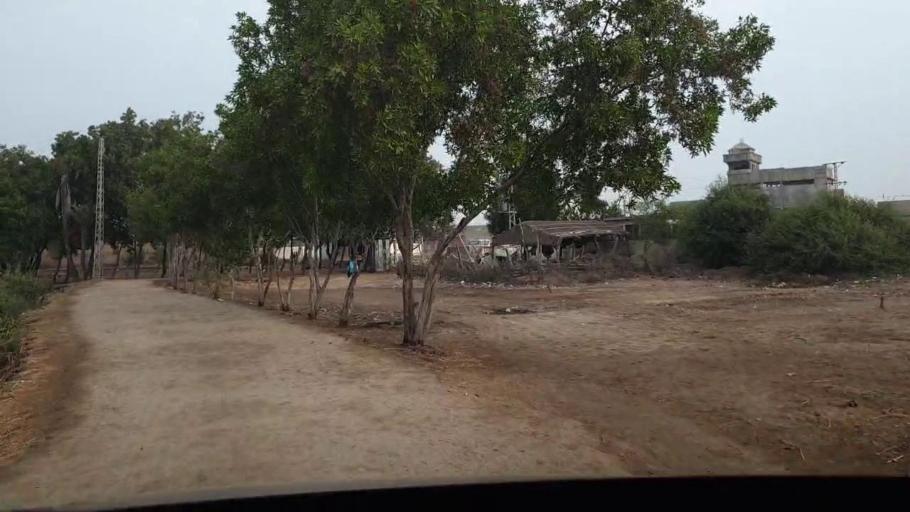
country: PK
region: Sindh
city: Thatta
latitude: 24.5982
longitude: 68.0824
